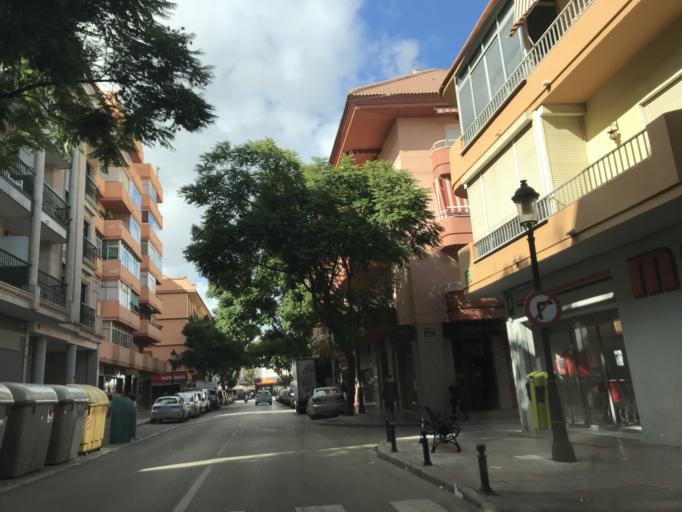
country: ES
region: Andalusia
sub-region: Provincia de Malaga
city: Fuengirola
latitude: 36.5398
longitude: -4.6294
